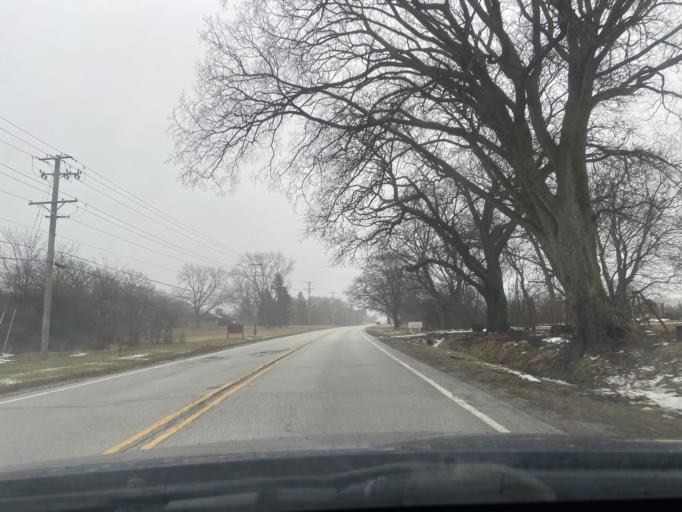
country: US
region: Illinois
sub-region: Lake County
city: Volo
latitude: 42.3206
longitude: -88.1407
